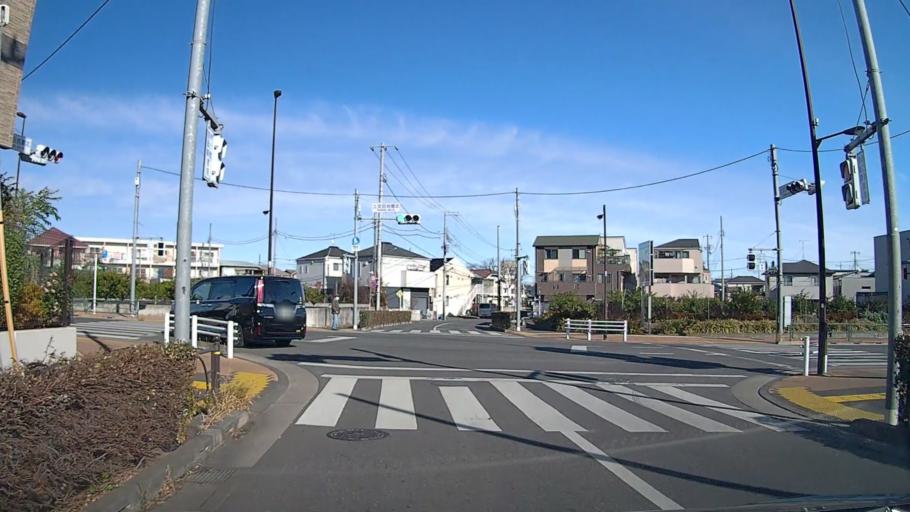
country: JP
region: Saitama
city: Wako
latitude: 35.7615
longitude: 139.6129
